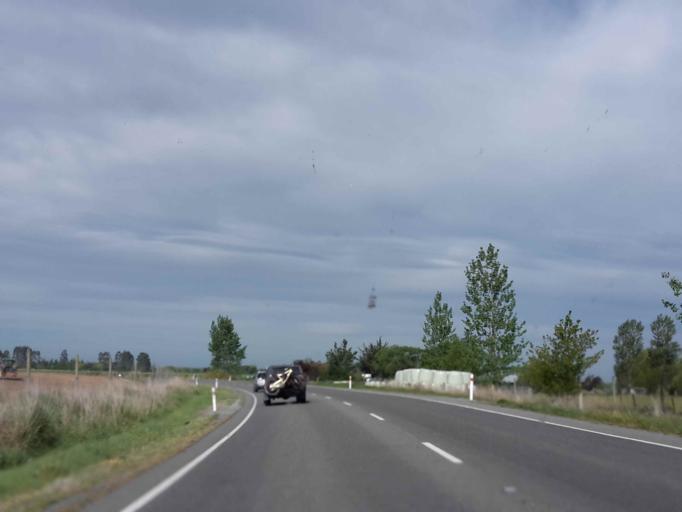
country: NZ
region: Canterbury
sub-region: Timaru District
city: Pleasant Point
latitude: -44.1209
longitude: 171.1916
